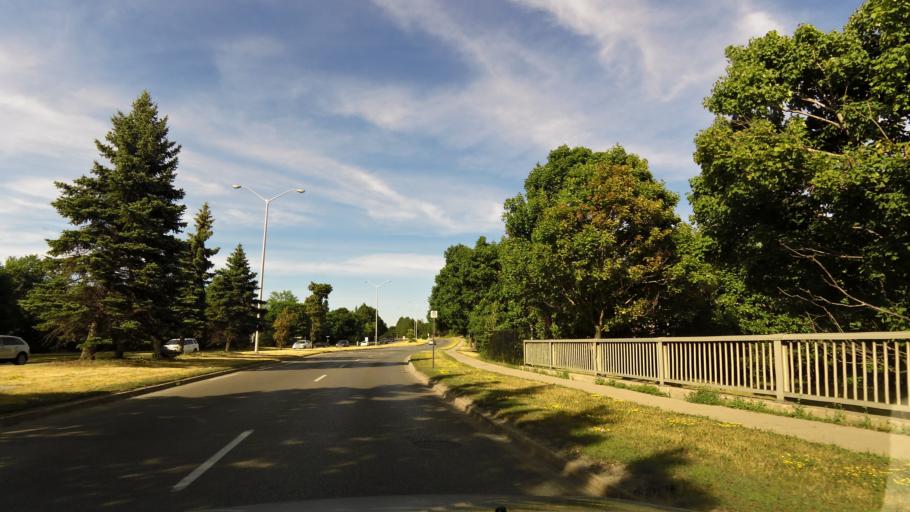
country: CA
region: Ontario
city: Brampton
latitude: 43.7306
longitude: -79.7893
